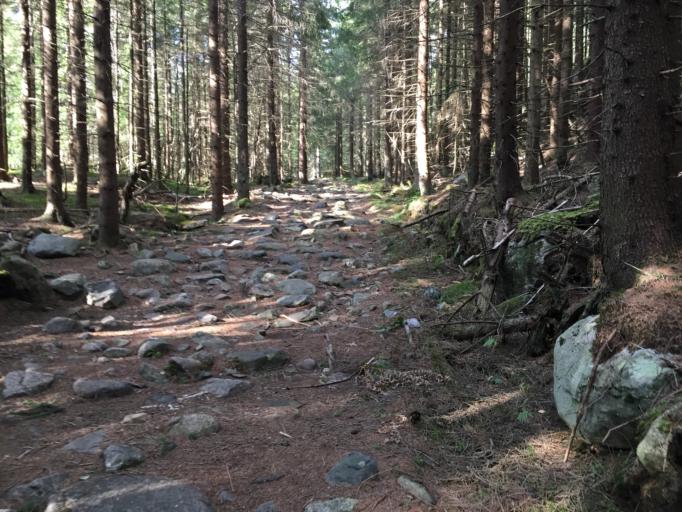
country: NO
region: Akershus
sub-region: Raelingen
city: Fjerdingby
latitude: 59.9129
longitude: 11.0288
